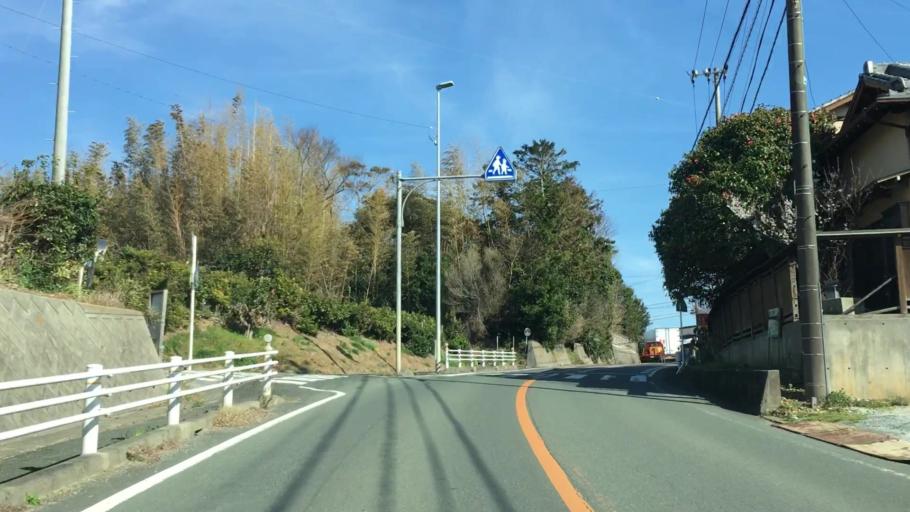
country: JP
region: Shizuoka
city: Kosai-shi
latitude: 34.6829
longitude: 137.4803
